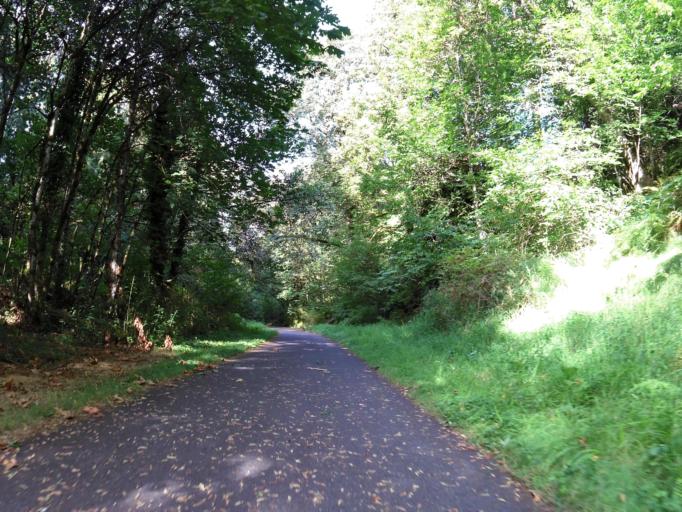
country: US
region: Washington
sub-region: Thurston County
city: Olympia
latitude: 47.0372
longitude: -122.8707
